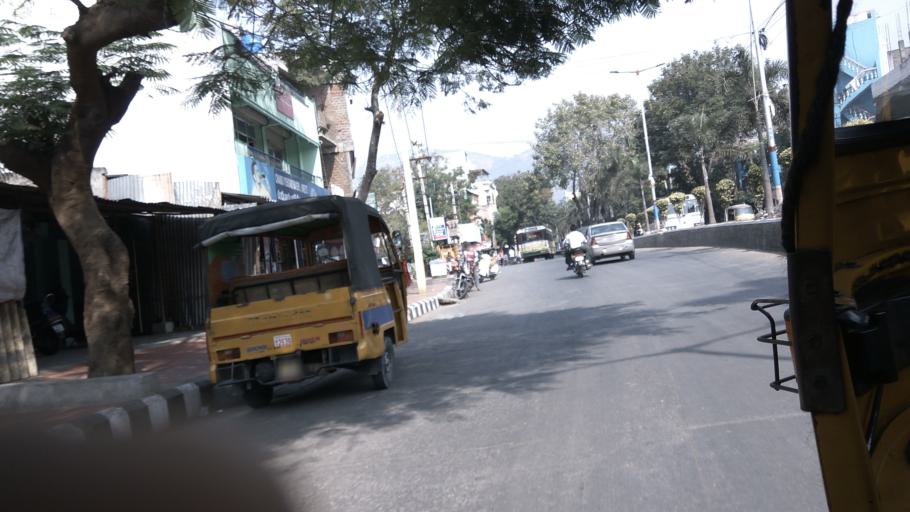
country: IN
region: Andhra Pradesh
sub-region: Chittoor
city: Tirupati
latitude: 13.6351
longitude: 79.4129
